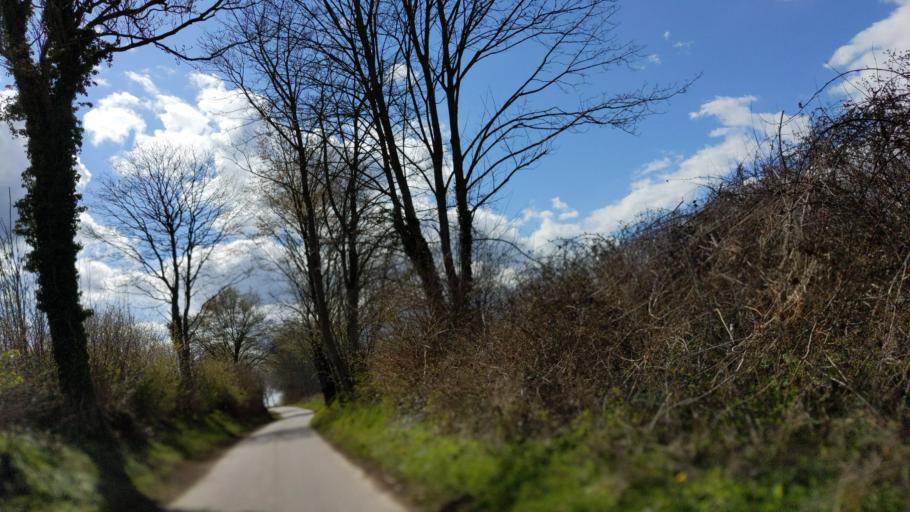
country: DE
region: Mecklenburg-Vorpommern
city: Selmsdorf
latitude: 53.8845
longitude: 10.8881
